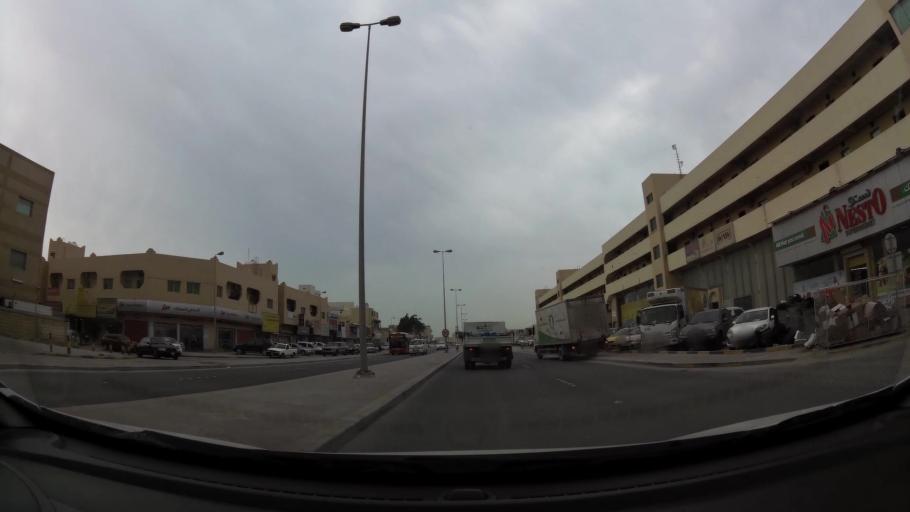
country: BH
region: Northern
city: Madinat `Isa
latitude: 26.1866
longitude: 50.5309
